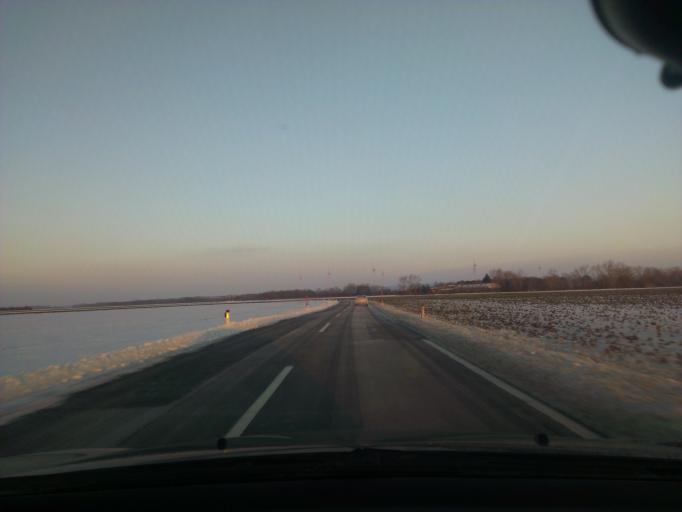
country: AT
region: Lower Austria
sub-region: Politischer Bezirk Baden
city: Mitterndorf an der Fischa
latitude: 47.9616
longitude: 16.4485
